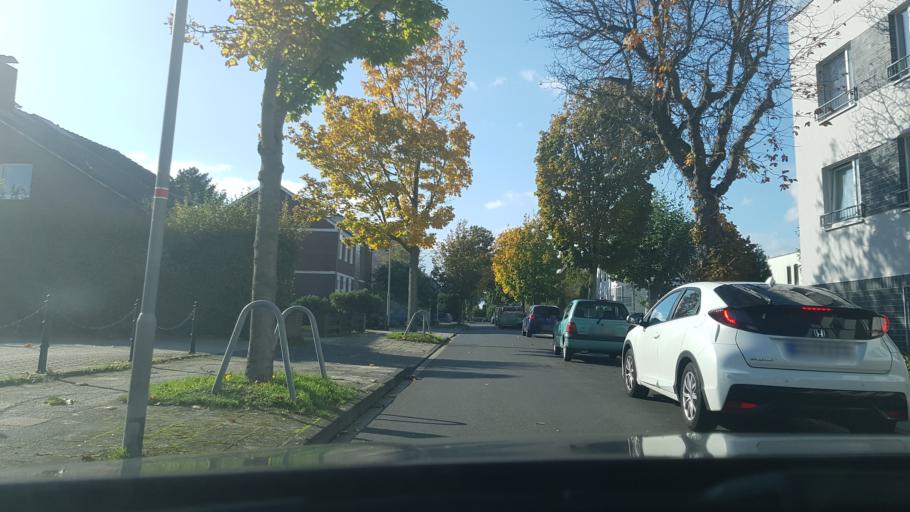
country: DE
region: North Rhine-Westphalia
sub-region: Regierungsbezirk Dusseldorf
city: Moers
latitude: 51.4153
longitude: 6.5939
